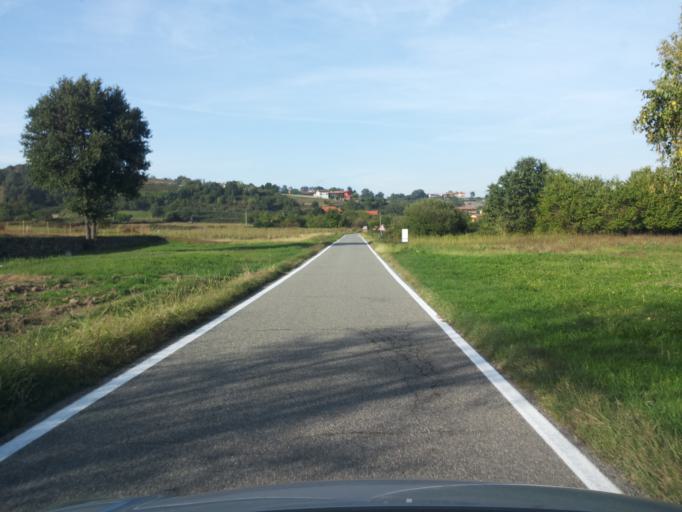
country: IT
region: Piedmont
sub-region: Provincia di Biella
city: Dorzano
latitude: 45.4349
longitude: 8.0962
